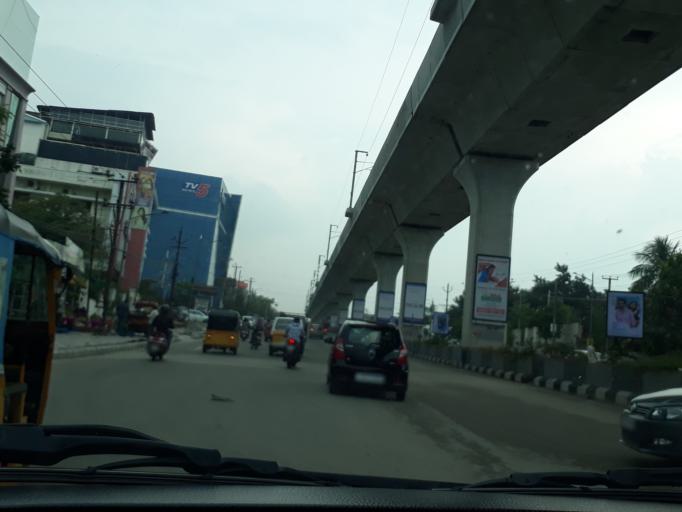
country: IN
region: Telangana
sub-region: Rangareddi
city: Kukatpalli
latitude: 17.4293
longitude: 78.4183
